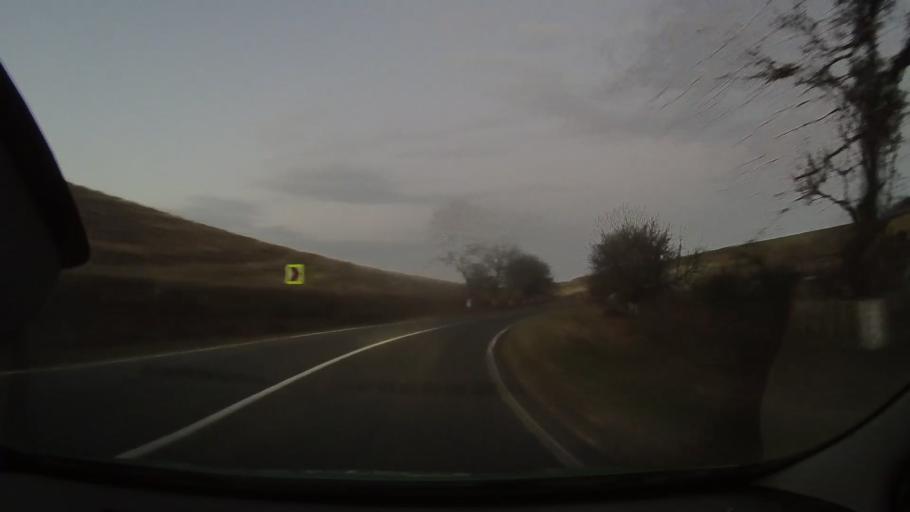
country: RO
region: Constanta
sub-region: Comuna Ion Corvin
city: Ion Corvin
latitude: 44.1034
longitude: 27.7549
